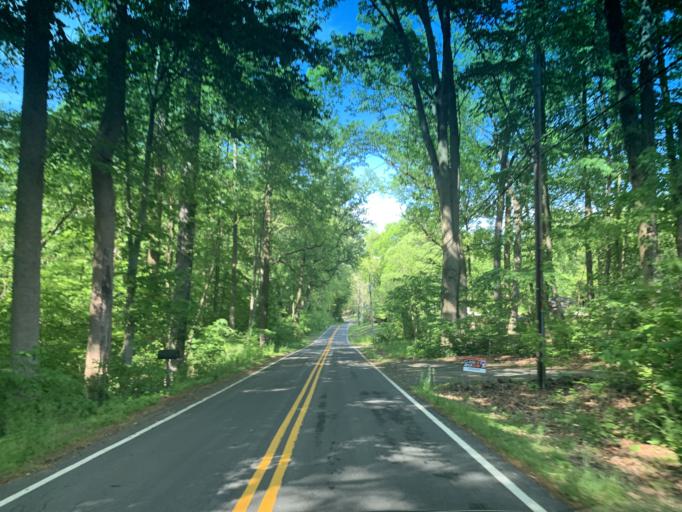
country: US
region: Maryland
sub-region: Cecil County
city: Rising Sun
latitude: 39.6870
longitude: -76.1889
